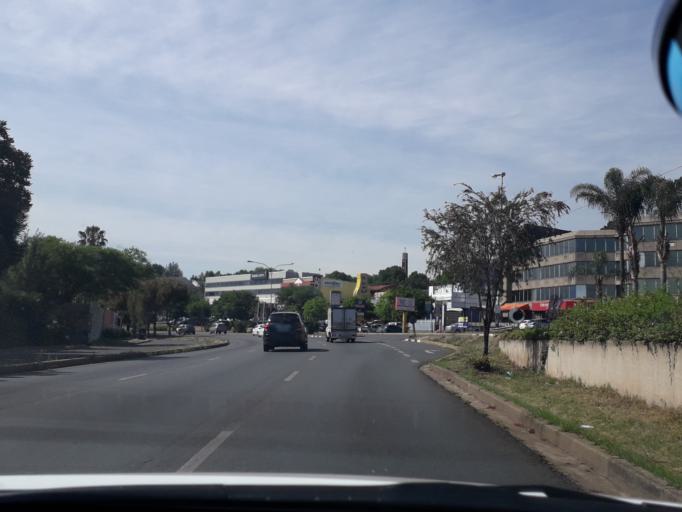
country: ZA
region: Gauteng
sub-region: City of Johannesburg Metropolitan Municipality
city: Johannesburg
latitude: -26.1427
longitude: 27.9796
